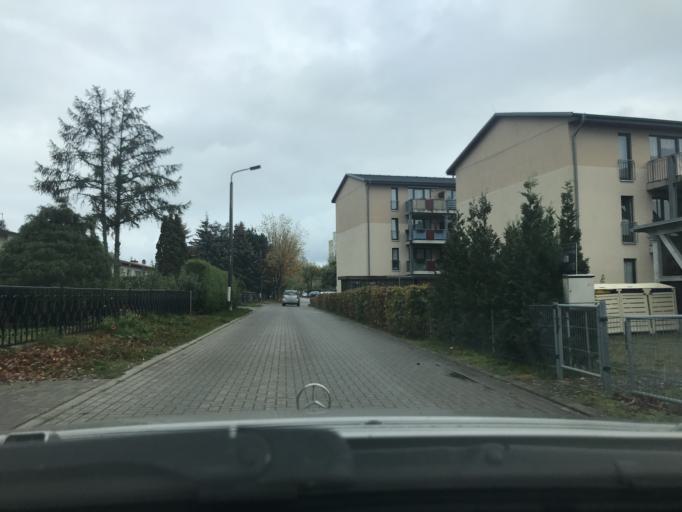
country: DE
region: Mecklenburg-Vorpommern
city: Ostseebad Zinnowitz
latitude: 54.0783
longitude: 13.8979
